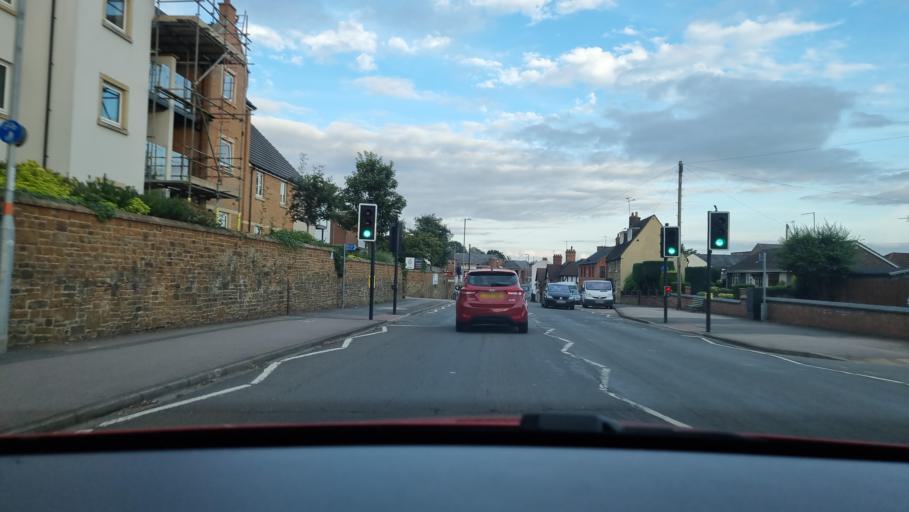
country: GB
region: England
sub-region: Northamptonshire
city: Northampton
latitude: 52.2650
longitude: -0.9031
